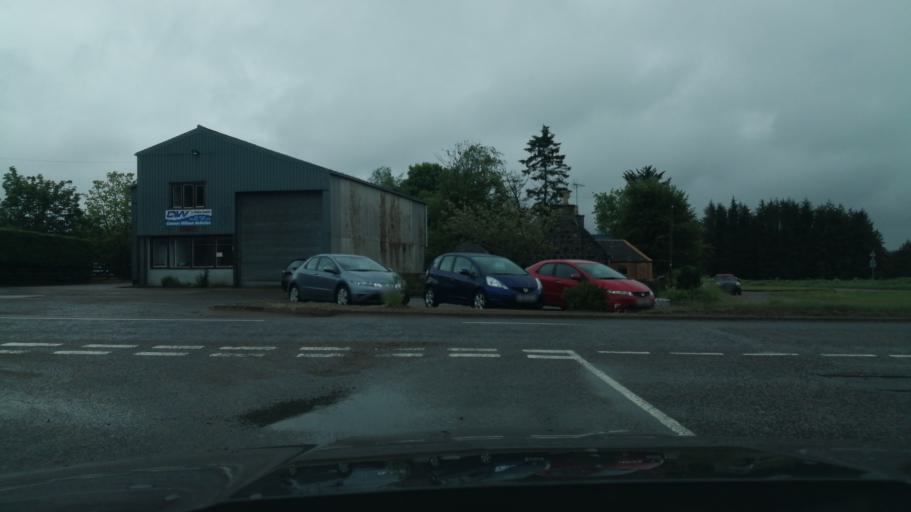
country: GB
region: Scotland
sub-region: Aberdeenshire
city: Huntly
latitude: 57.5339
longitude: -2.7683
